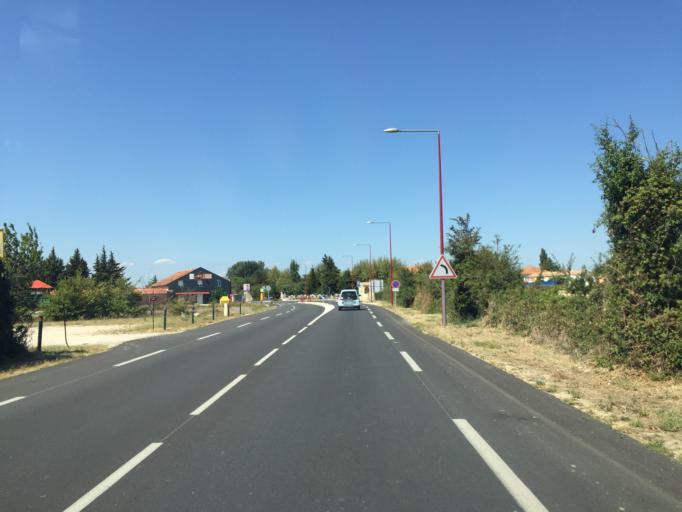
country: FR
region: Provence-Alpes-Cote d'Azur
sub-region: Departement du Vaucluse
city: Jonquieres
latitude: 44.1161
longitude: 4.8890
